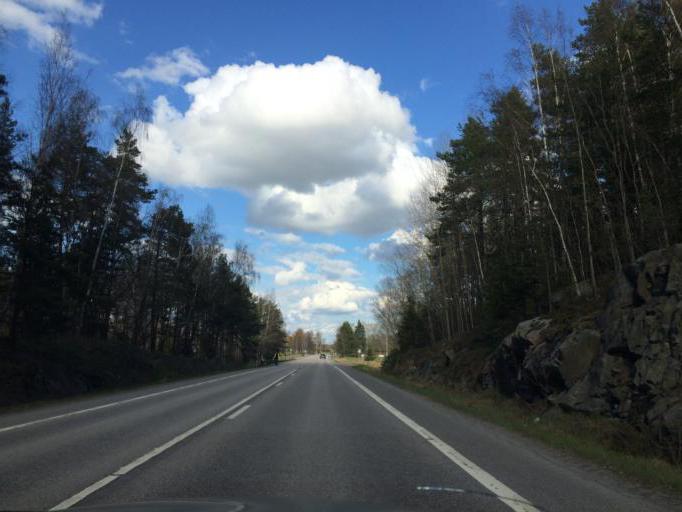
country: SE
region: Soedermanland
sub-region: Eskilstuna Kommun
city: Eskilstuna
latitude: 59.3982
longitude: 16.5546
